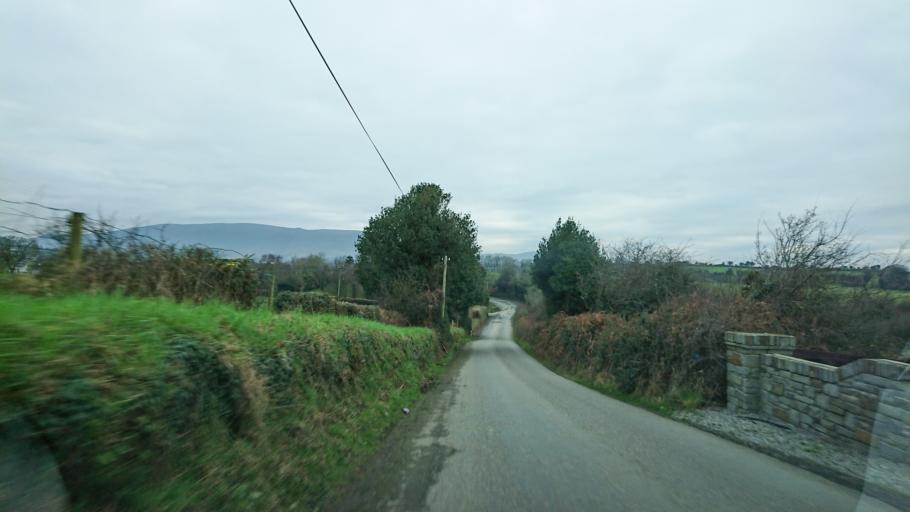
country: IE
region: Munster
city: Carrick-on-Suir
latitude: 52.2760
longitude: -7.4137
